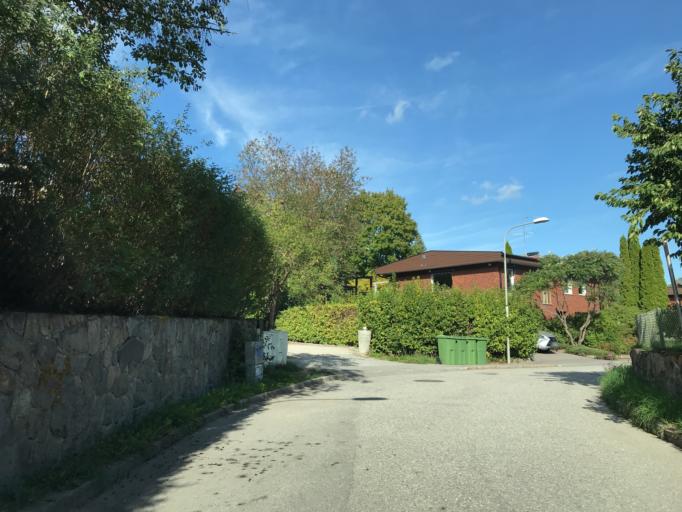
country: SE
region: Stockholm
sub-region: Huddinge Kommun
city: Segeltorp
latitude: 59.2755
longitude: 17.9560
